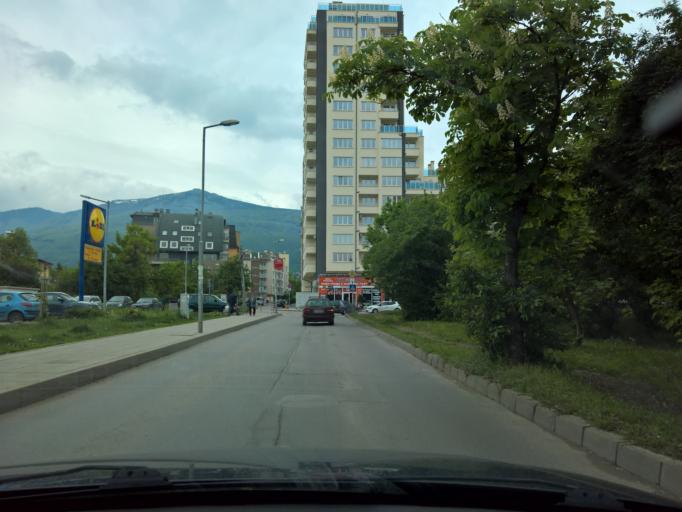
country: BG
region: Sofia-Capital
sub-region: Stolichna Obshtina
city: Sofia
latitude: 42.6596
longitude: 23.2998
